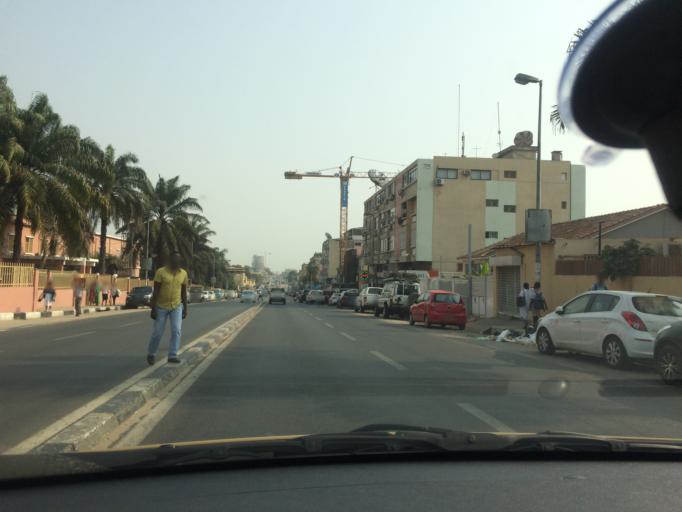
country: AO
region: Luanda
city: Luanda
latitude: -8.8265
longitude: 13.2236
